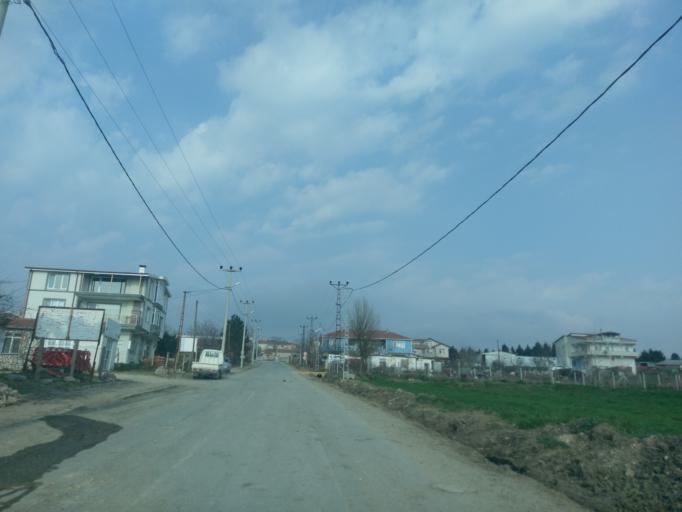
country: TR
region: Istanbul
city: Kavakli
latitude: 41.1256
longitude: 28.3200
